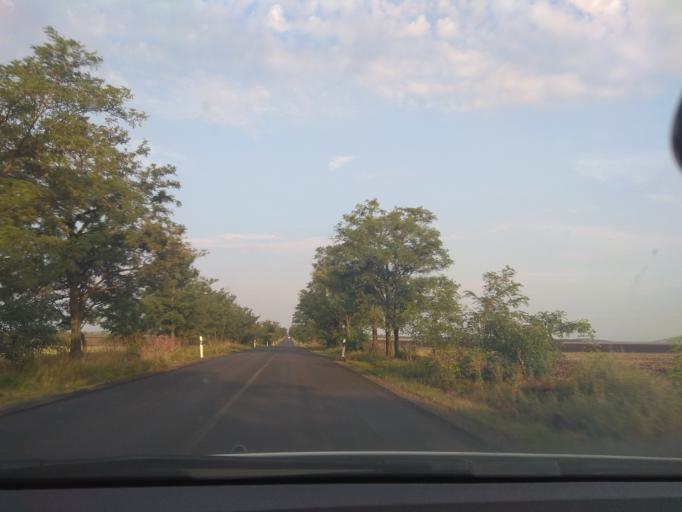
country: HU
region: Borsod-Abauj-Zemplen
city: Mezokovesd
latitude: 47.8144
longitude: 20.5249
